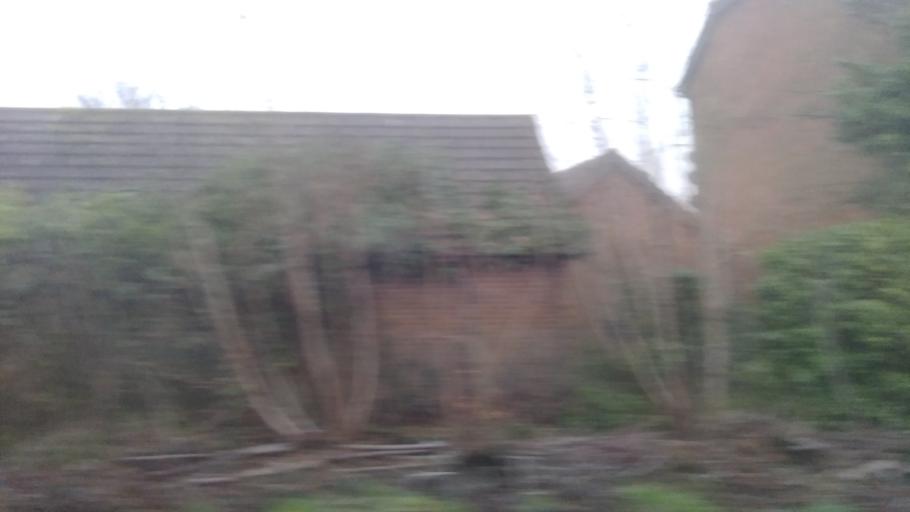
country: GB
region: England
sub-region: Kent
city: Folkestone
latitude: 51.0872
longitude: 1.1878
